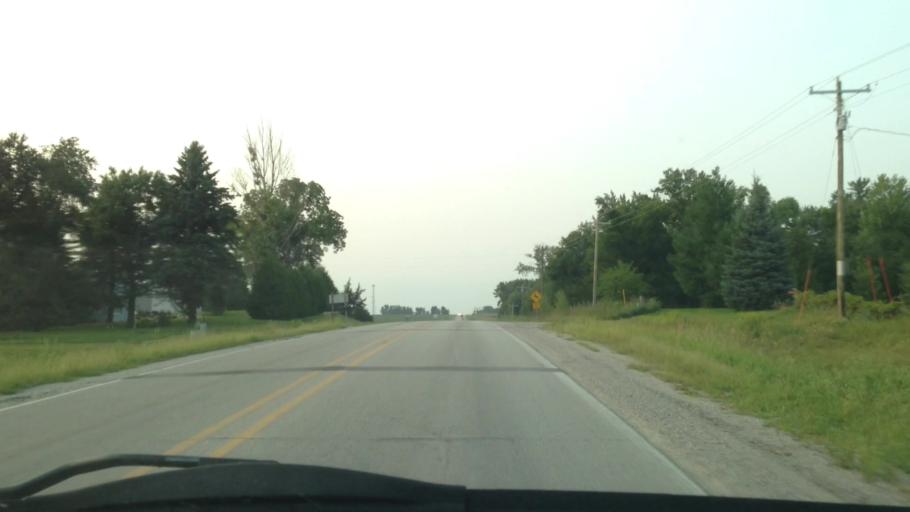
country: US
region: Iowa
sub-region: Benton County
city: Atkins
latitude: 42.0662
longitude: -91.8691
